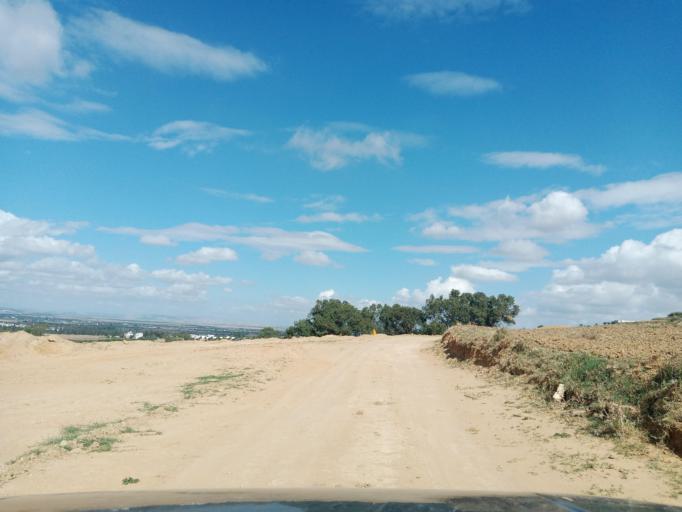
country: TN
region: Tunis
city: Oued Lill
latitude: 36.8139
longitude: 9.9982
